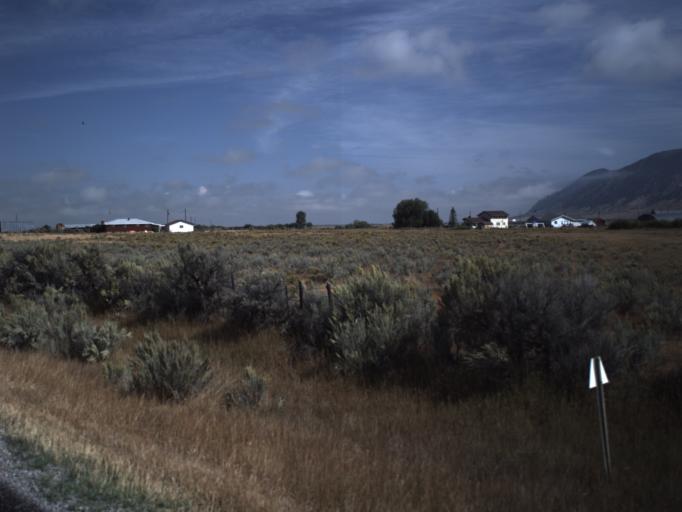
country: US
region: Utah
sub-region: Rich County
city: Randolph
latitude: 41.5957
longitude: -111.1737
